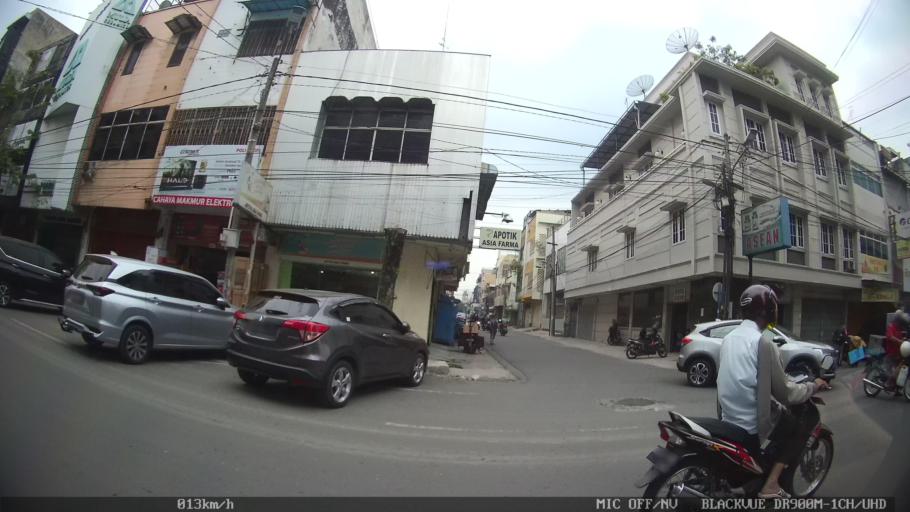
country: ID
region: North Sumatra
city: Medan
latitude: 3.5837
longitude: 98.6905
